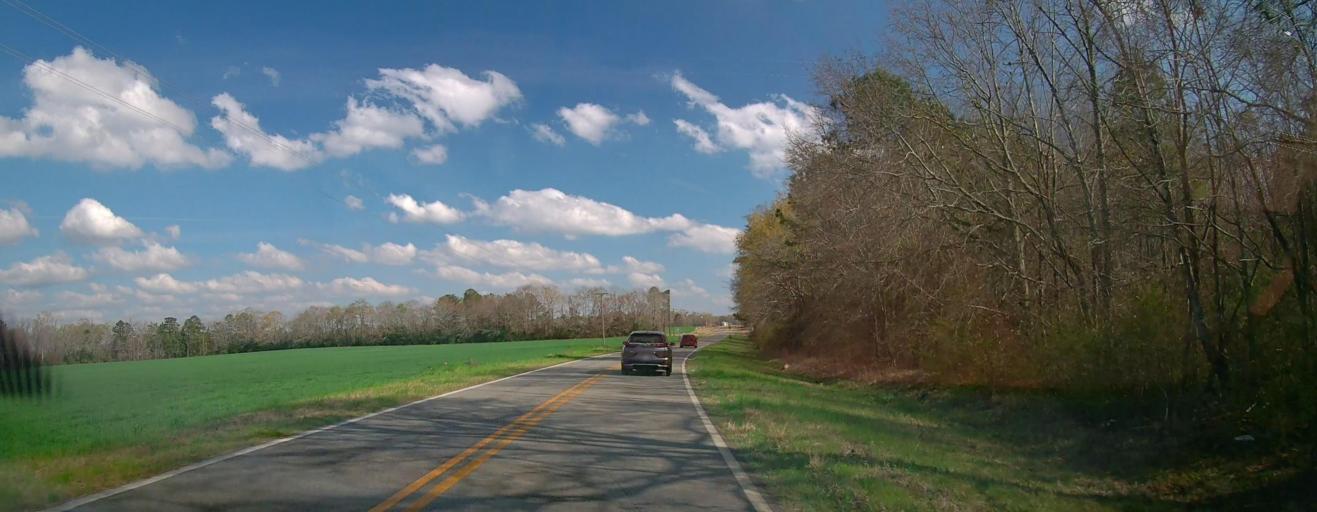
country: US
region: Georgia
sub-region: Wilkinson County
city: Irwinton
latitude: 32.6323
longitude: -83.1030
